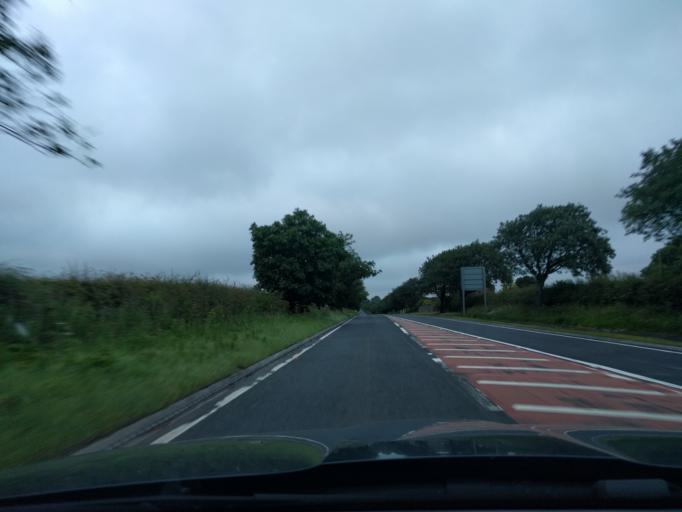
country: GB
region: England
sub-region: Northumberland
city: Hebron
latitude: 55.2283
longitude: -1.7052
